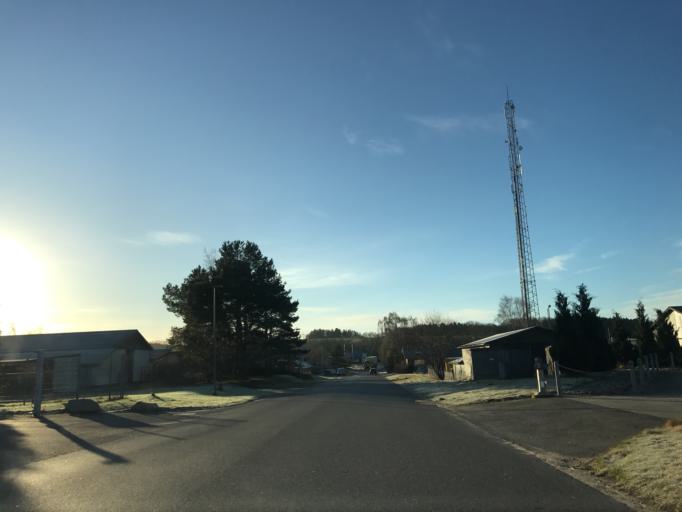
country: DK
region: Central Jutland
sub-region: Silkeborg Kommune
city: Svejbaek
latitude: 56.1559
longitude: 9.6454
